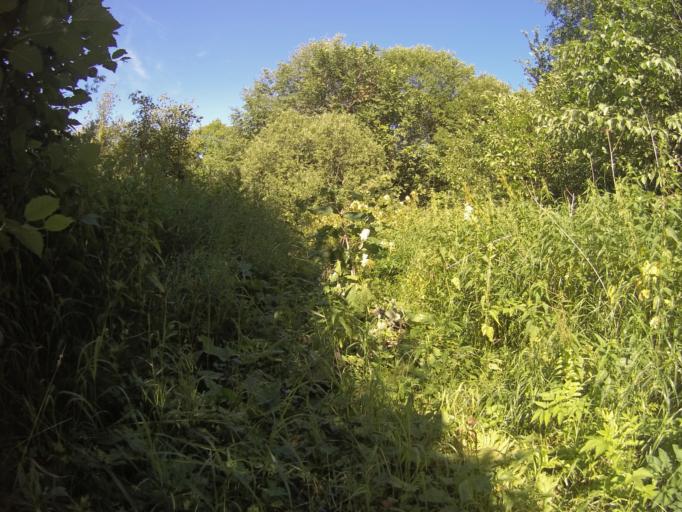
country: RU
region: Vladimir
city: Raduzhnyy
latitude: 56.0505
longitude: 40.3436
